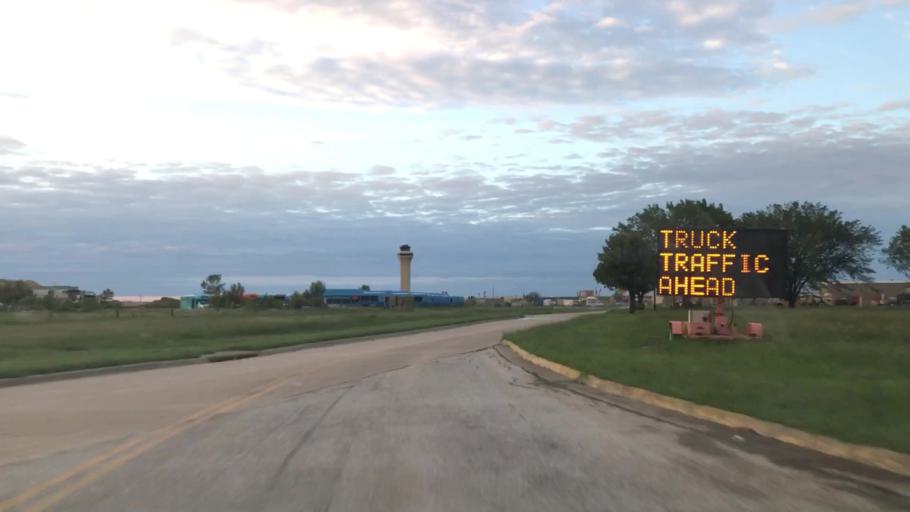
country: US
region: Texas
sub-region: Dallas County
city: Coppell
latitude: 32.8883
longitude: -97.0157
